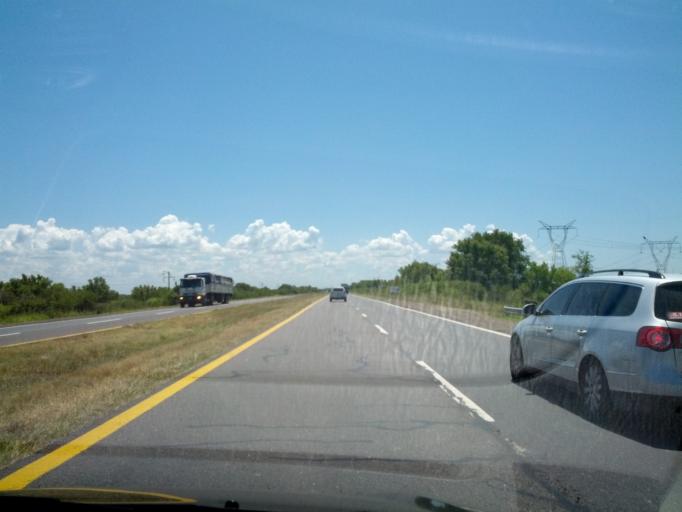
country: AR
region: Entre Rios
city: Villa Paranacito
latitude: -33.7658
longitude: -58.8651
